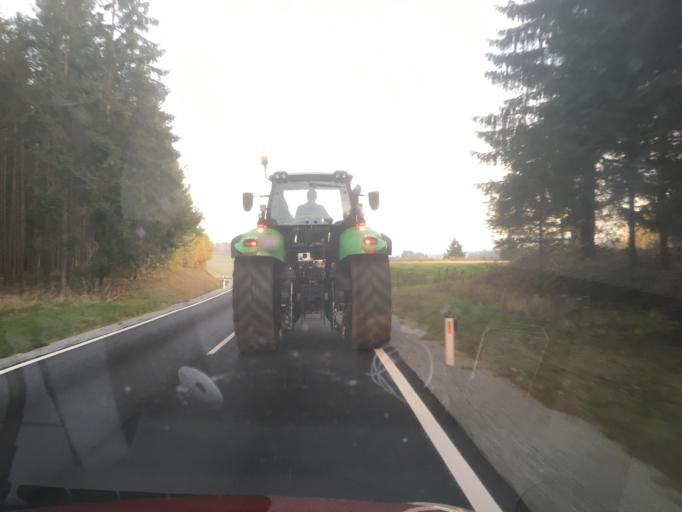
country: AT
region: Lower Austria
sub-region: Politischer Bezirk Zwettl
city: Langschlag
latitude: 48.5701
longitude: 14.9136
